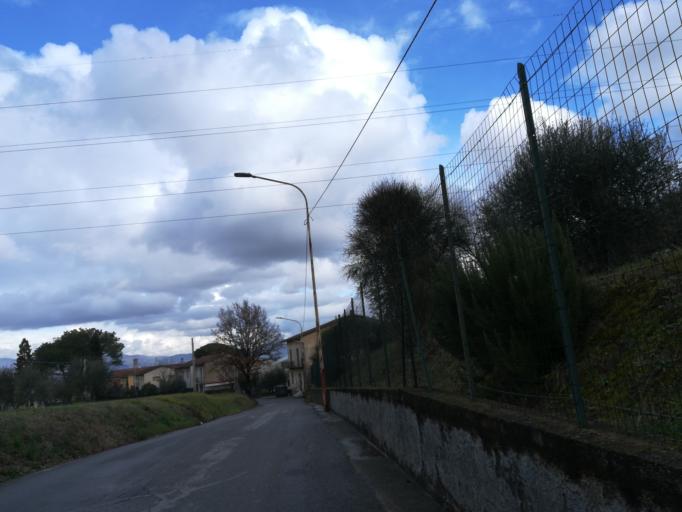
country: IT
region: Tuscany
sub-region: Provincia di Prato
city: Poggio A Caiano
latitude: 43.8079
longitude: 11.0517
